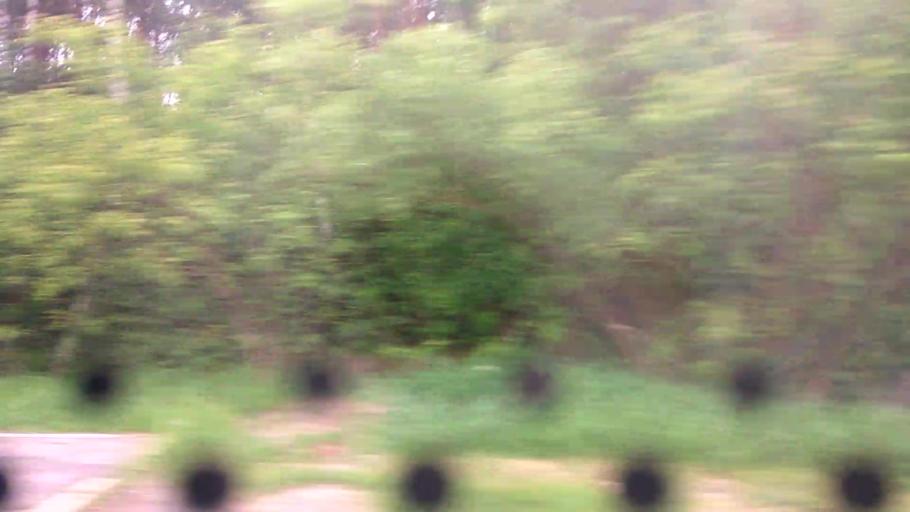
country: RU
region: Moskovskaya
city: Kolomna
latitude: 55.0521
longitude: 38.8711
